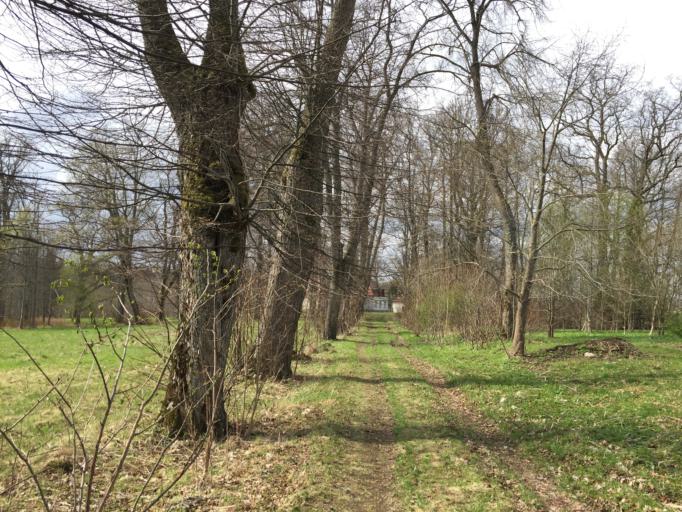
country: LV
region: Ligatne
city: Ligatne
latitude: 57.2175
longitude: 25.0681
